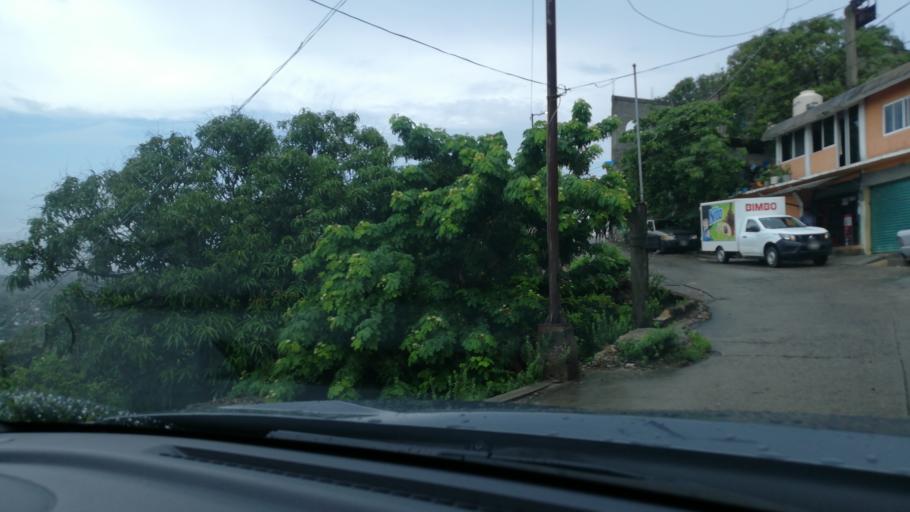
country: MX
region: Oaxaca
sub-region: Salina Cruz
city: Salina Cruz
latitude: 16.1865
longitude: -95.1928
